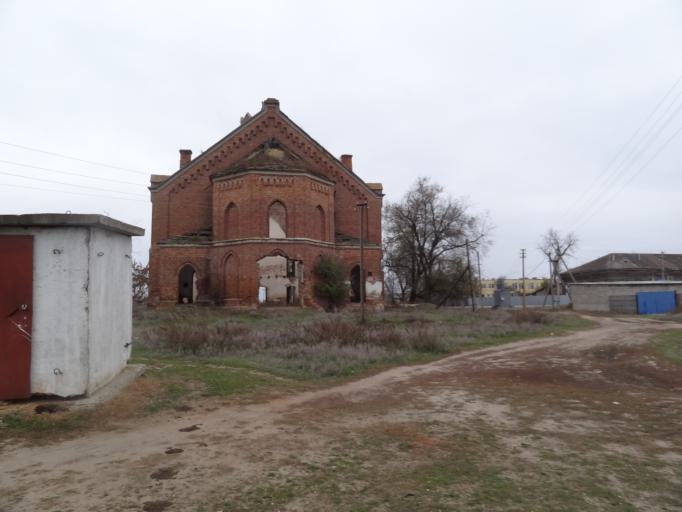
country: RU
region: Saratov
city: Sovetskoye
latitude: 51.5325
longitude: 46.6115
